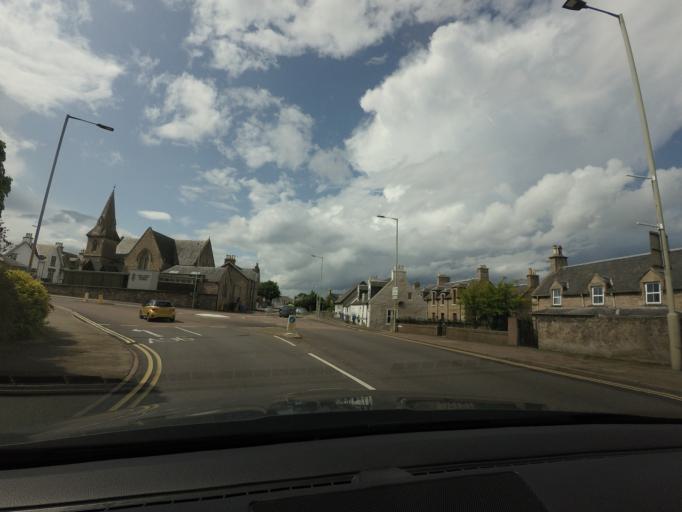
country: GB
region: Scotland
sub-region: Highland
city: Nairn
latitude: 57.5866
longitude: -3.8678
